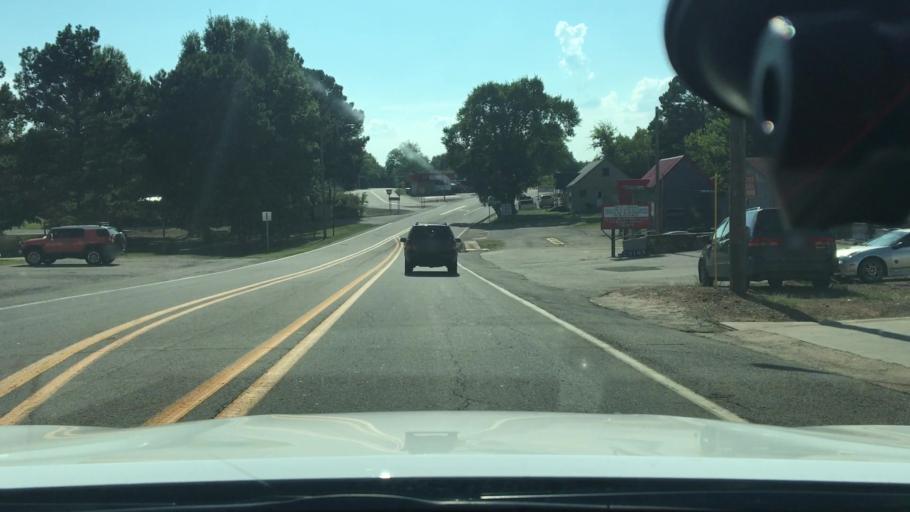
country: US
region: Arkansas
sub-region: Johnson County
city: Clarksville
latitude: 35.4715
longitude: -93.4794
